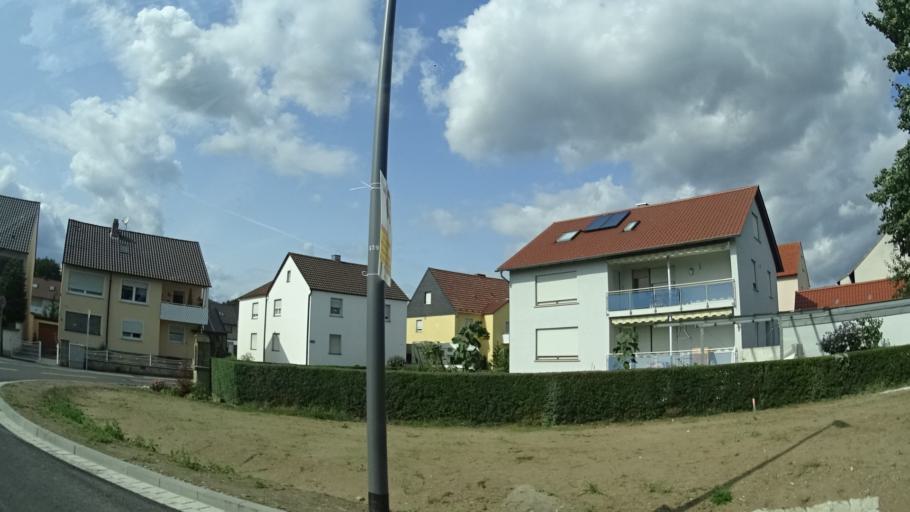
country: DE
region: Bavaria
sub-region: Regierungsbezirk Unterfranken
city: Rothlein
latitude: 49.9883
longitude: 10.2204
